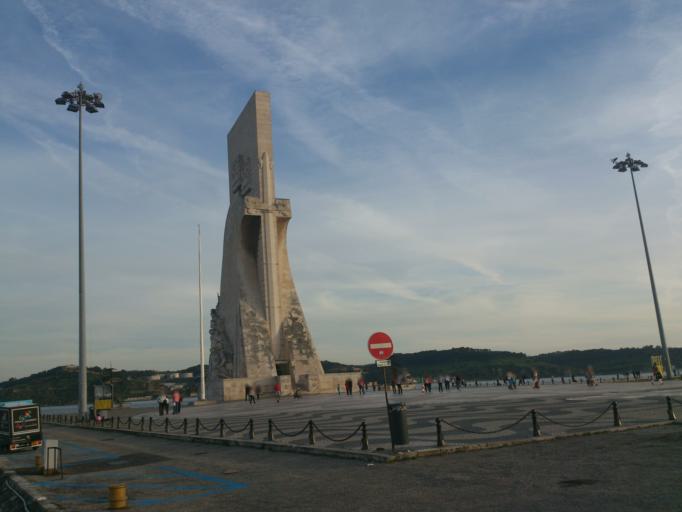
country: PT
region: Lisbon
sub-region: Oeiras
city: Alges
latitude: 38.6946
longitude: -9.2057
